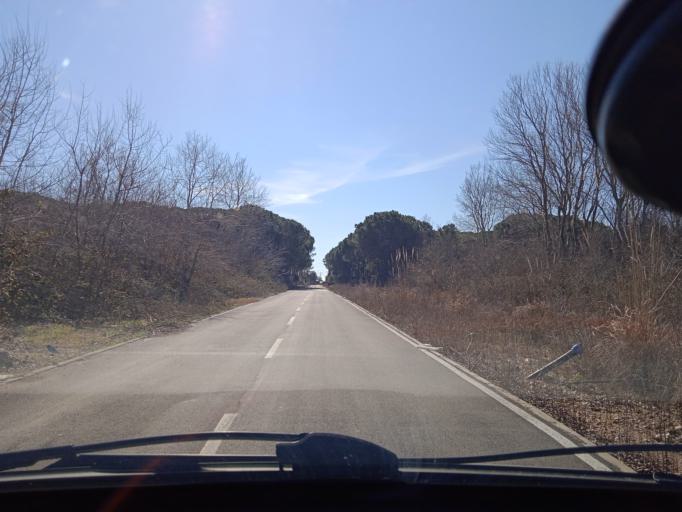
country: AL
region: Shkoder
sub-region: Rrethi i Shkodres
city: Velipoje
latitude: 41.8660
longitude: 19.4157
